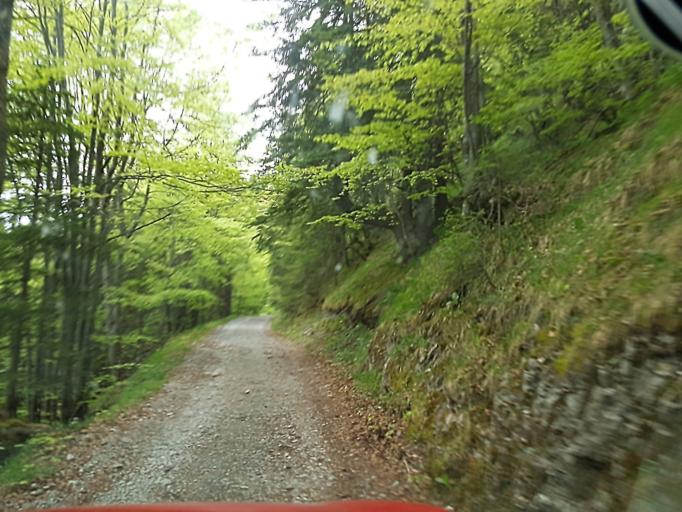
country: SK
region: Zilinsky
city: Ruzomberok
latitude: 49.0457
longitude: 19.2495
